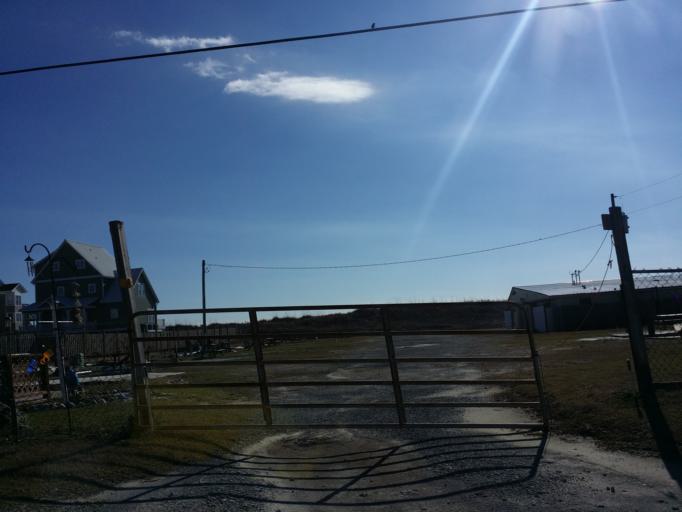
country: US
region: North Carolina
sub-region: Pender County
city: Surf City
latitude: 34.4521
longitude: -77.5021
